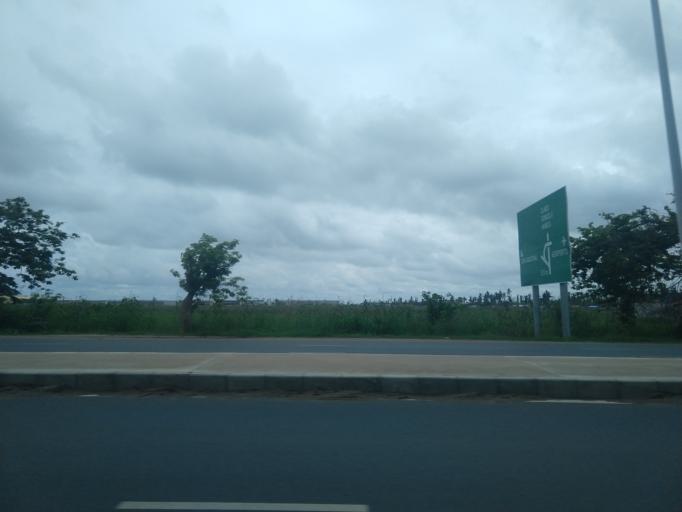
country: MZ
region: Sofala
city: Beira
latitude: -19.7870
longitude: 34.8753
